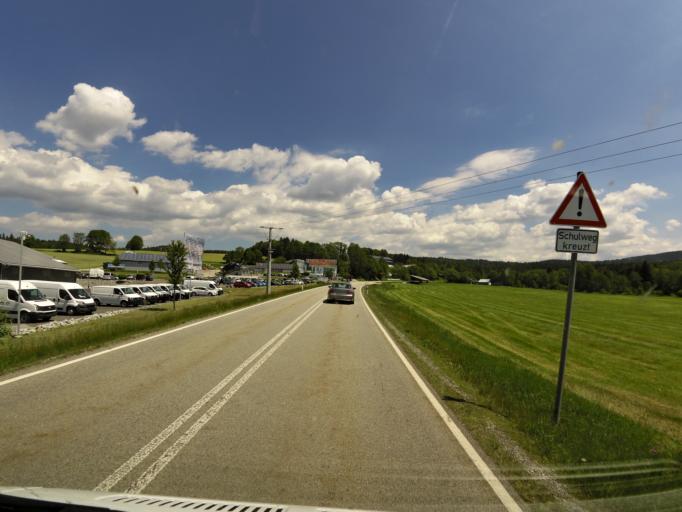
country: DE
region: Bavaria
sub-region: Lower Bavaria
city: Hinterschmiding
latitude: 48.8386
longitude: 13.5990
